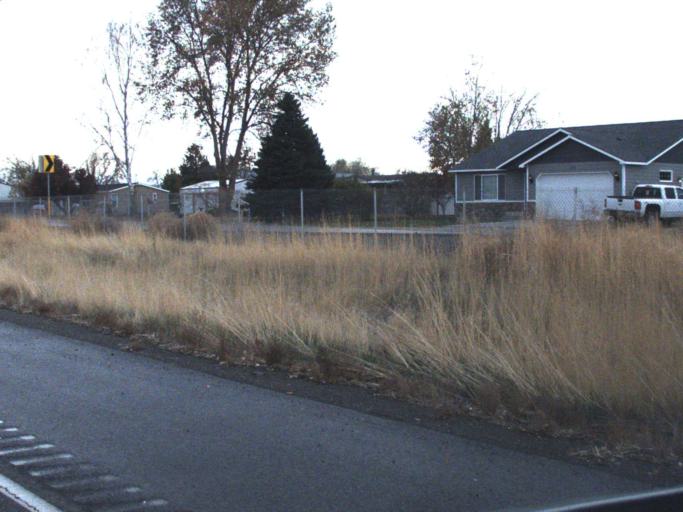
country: US
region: Washington
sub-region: Walla Walla County
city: Burbank
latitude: 46.1959
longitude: -118.9941
